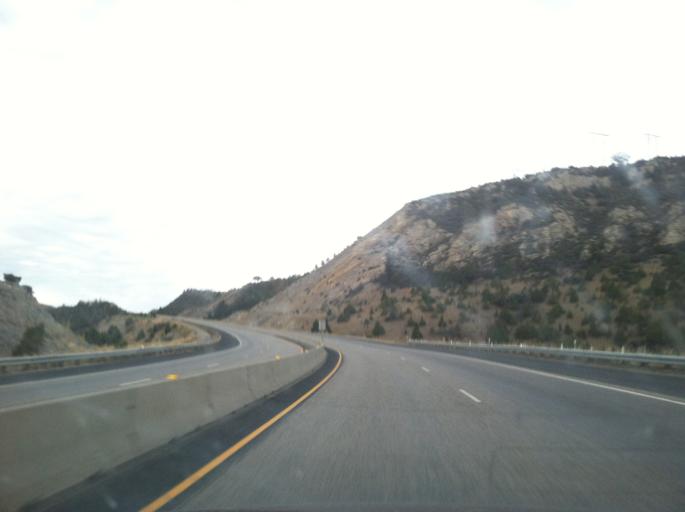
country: US
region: Montana
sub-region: Jefferson County
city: Whitehall
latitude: 45.8751
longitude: -111.8916
